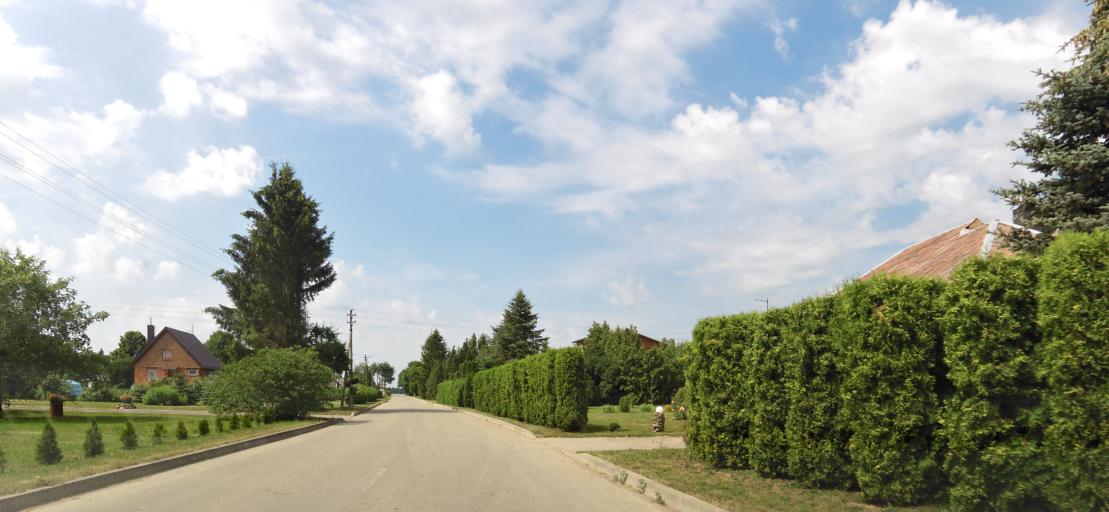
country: LT
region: Panevezys
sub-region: Birzai
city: Birzai
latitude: 56.2673
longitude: 24.6116
